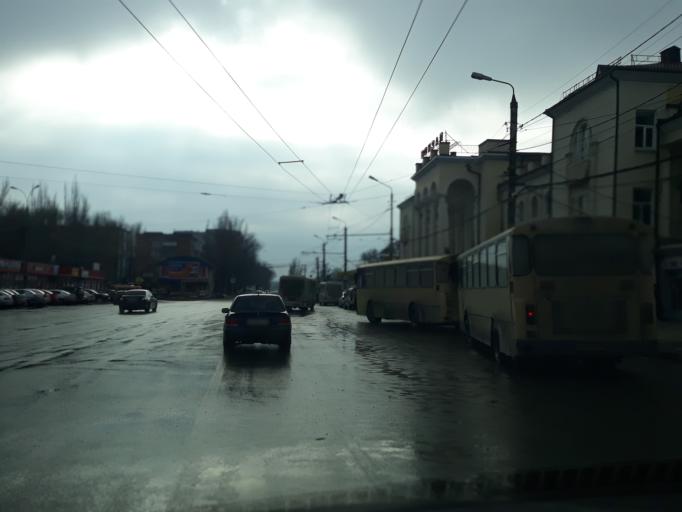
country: RU
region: Rostov
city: Taganrog
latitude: 47.2626
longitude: 38.9189
